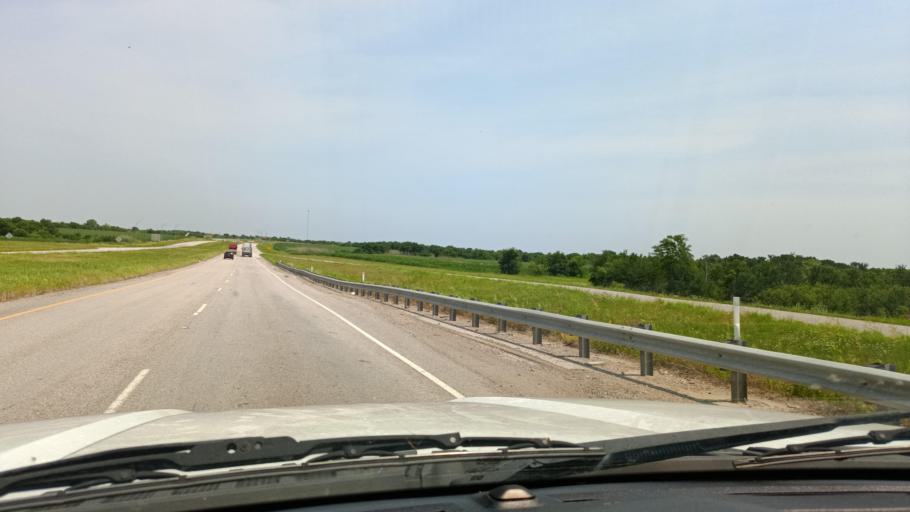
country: US
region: Texas
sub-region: Bell County
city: Little River-Academy
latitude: 31.0131
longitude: -97.3045
